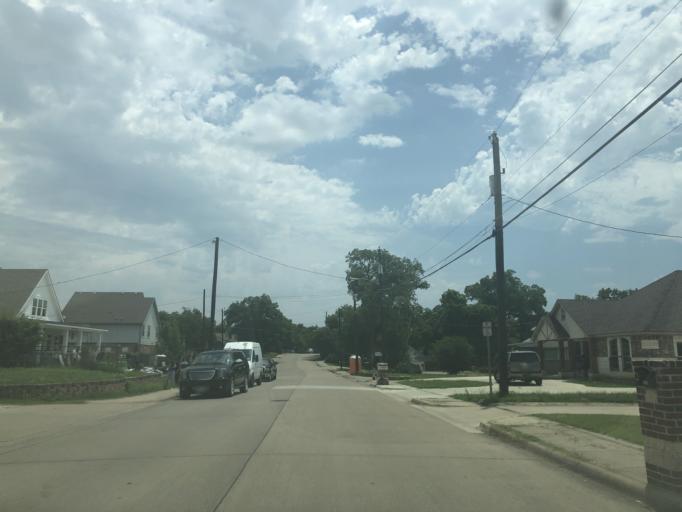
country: US
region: Texas
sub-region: Dallas County
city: Irving
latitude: 32.7939
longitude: -96.9337
